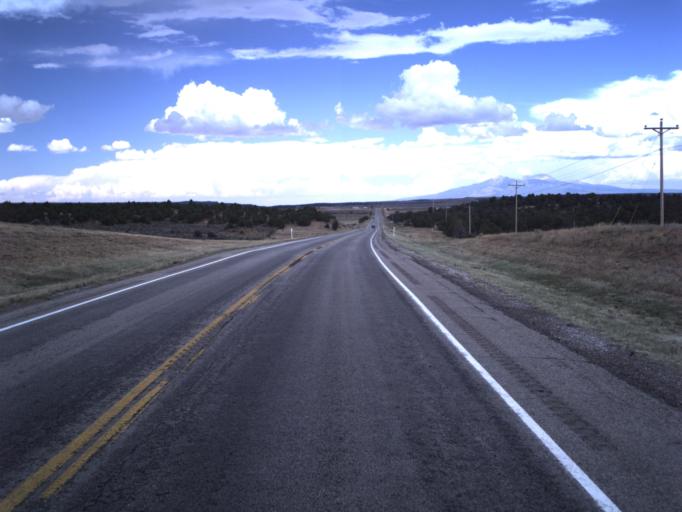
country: US
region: Utah
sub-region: San Juan County
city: Monticello
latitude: 37.9090
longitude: -109.3460
